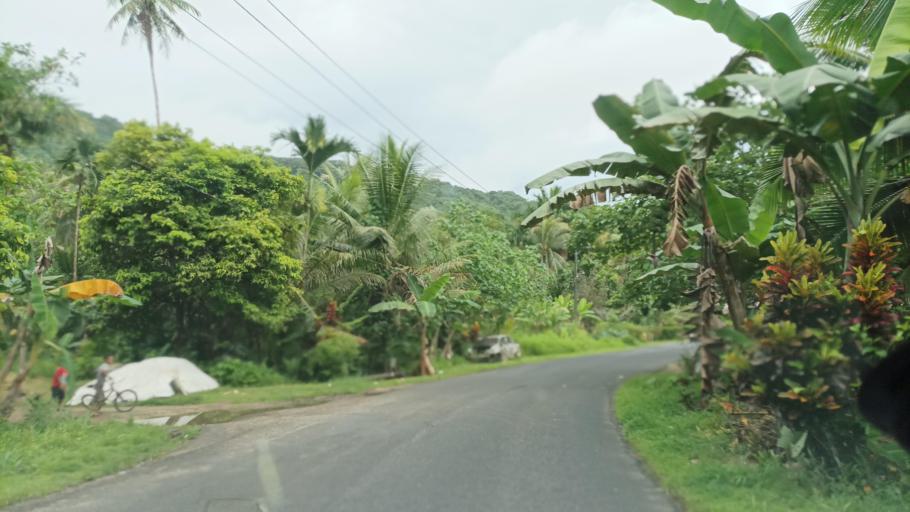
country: FM
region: Pohnpei
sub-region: Madolenihm Municipality
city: Madolenihm Municipality Government
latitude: 6.9135
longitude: 158.2996
